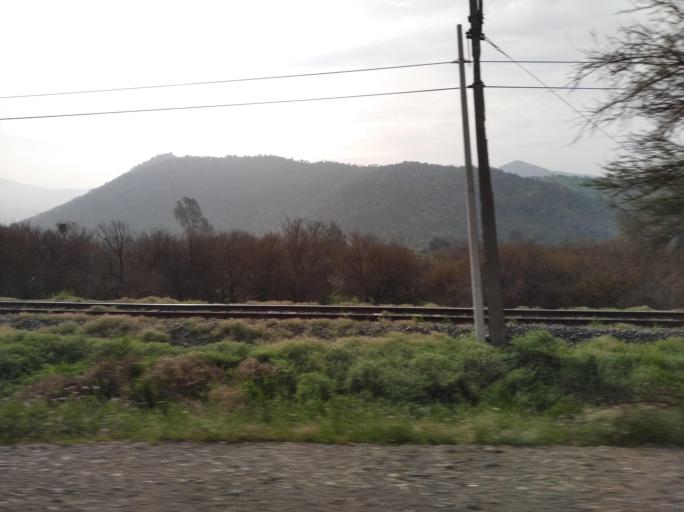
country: CL
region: Santiago Metropolitan
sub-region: Provincia de Chacabuco
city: Lampa
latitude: -33.1402
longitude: -70.9166
